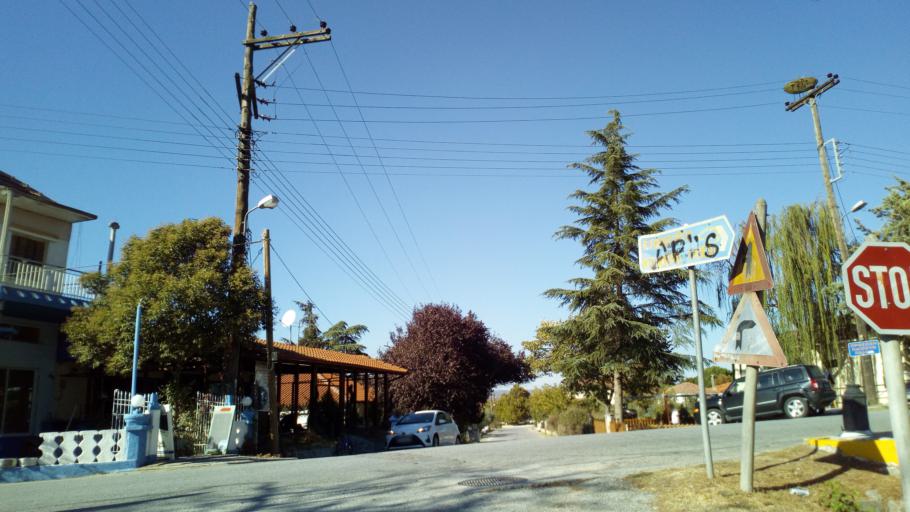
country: GR
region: Central Macedonia
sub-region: Nomos Thessalonikis
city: Gerakarou
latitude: 40.6350
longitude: 23.2453
